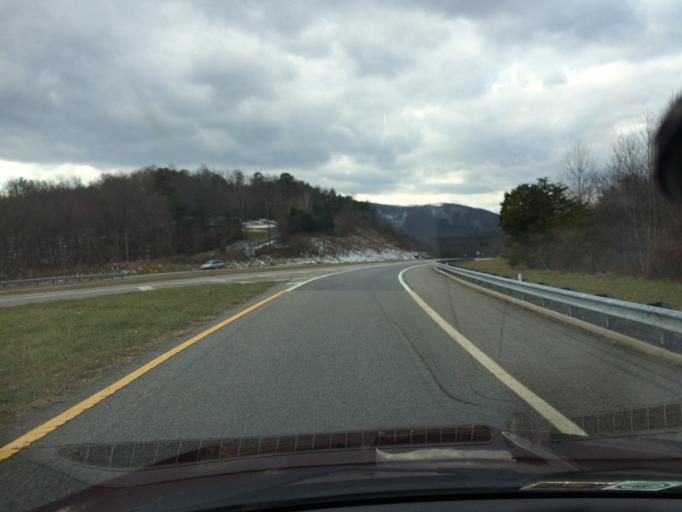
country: US
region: Virginia
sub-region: Patrick County
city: Stuart
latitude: 36.6507
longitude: -80.2721
